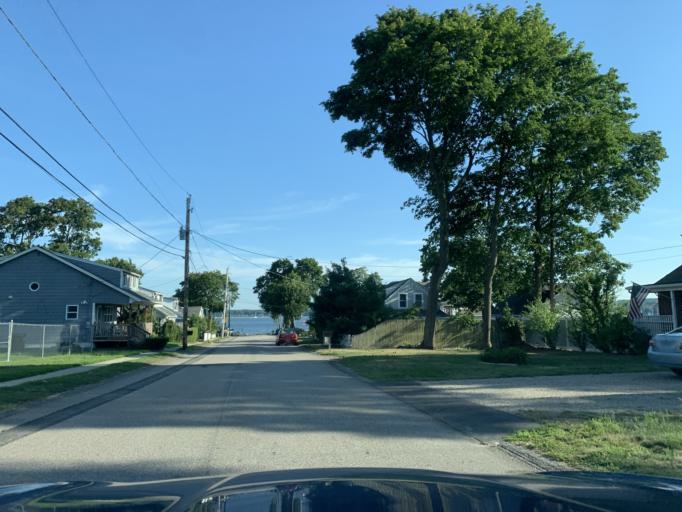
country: US
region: Rhode Island
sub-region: Kent County
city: Warwick
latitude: 41.6885
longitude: -71.4382
